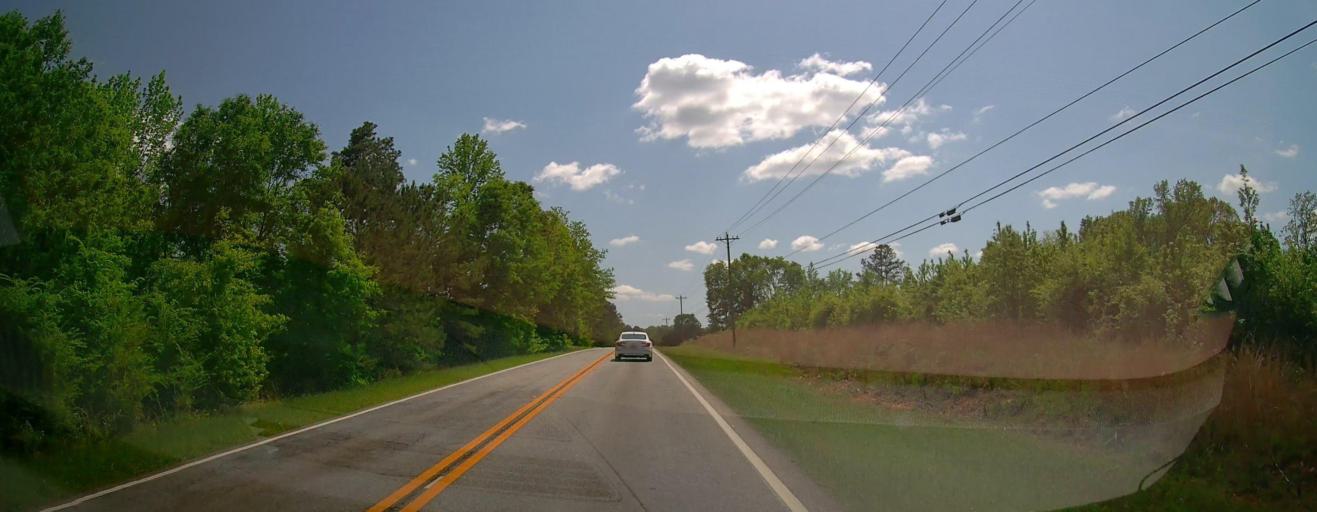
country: US
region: Georgia
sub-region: Putnam County
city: Eatonton
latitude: 33.3248
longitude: -83.2956
